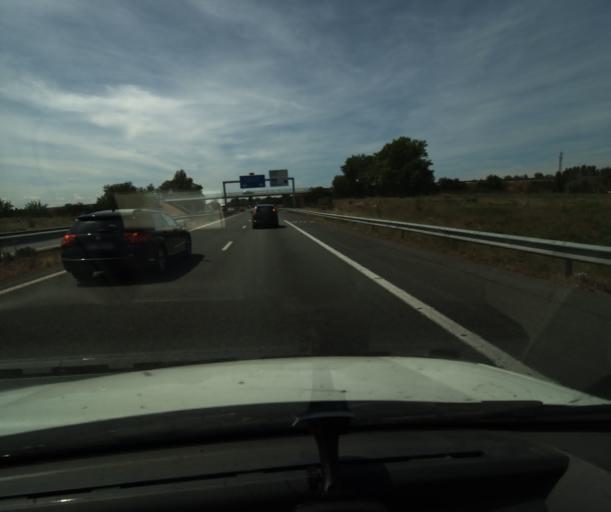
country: FR
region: Languedoc-Roussillon
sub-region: Departement de l'Aude
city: Bram
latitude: 43.2347
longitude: 2.1026
